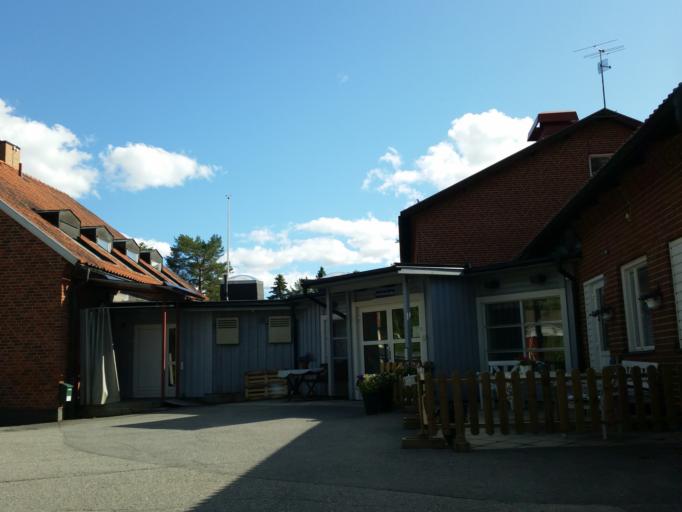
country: SE
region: Vaesterbotten
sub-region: Robertsfors Kommun
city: Robertsfors
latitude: 64.1961
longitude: 20.8497
